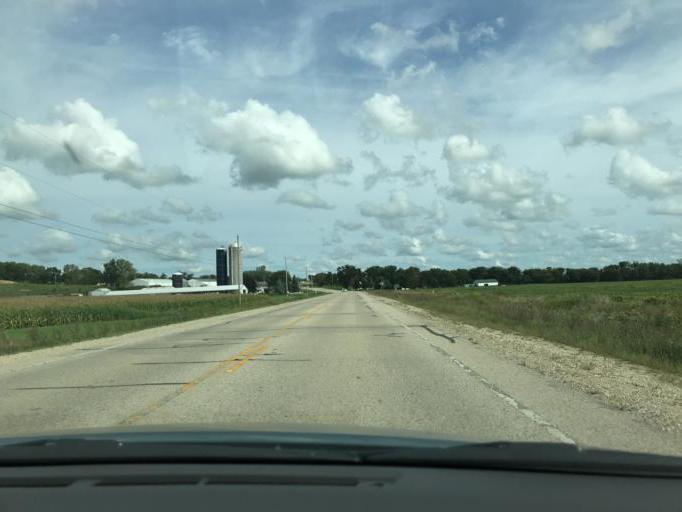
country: US
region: Wisconsin
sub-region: Racine County
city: Bohners Lake
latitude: 42.5922
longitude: -88.2220
